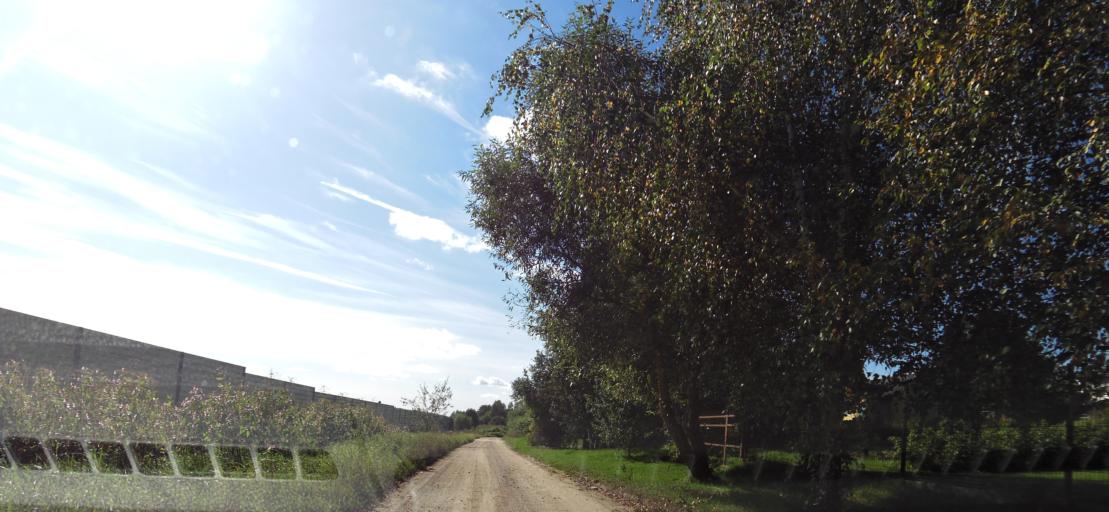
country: LT
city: Skaidiskes
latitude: 54.6368
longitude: 25.3616
